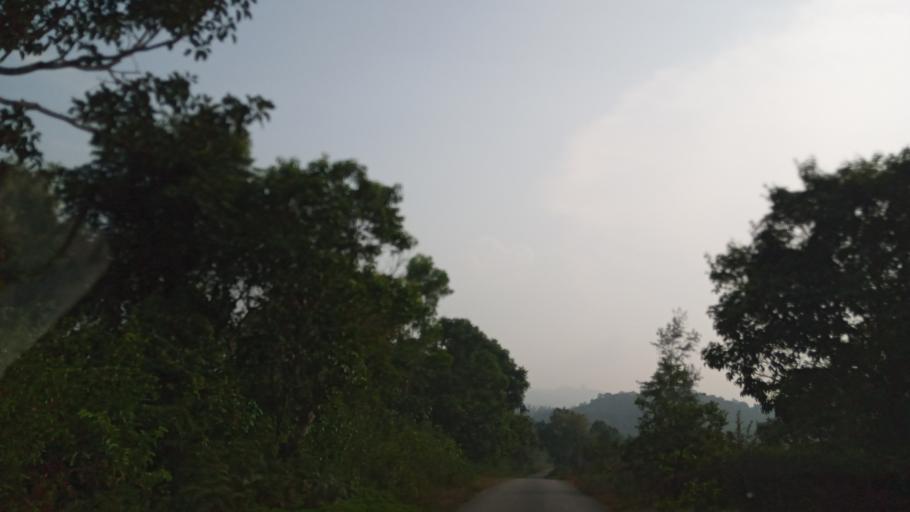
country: IN
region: Karnataka
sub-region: Chikmagalur
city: Mudigere
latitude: 13.0047
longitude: 75.6268
